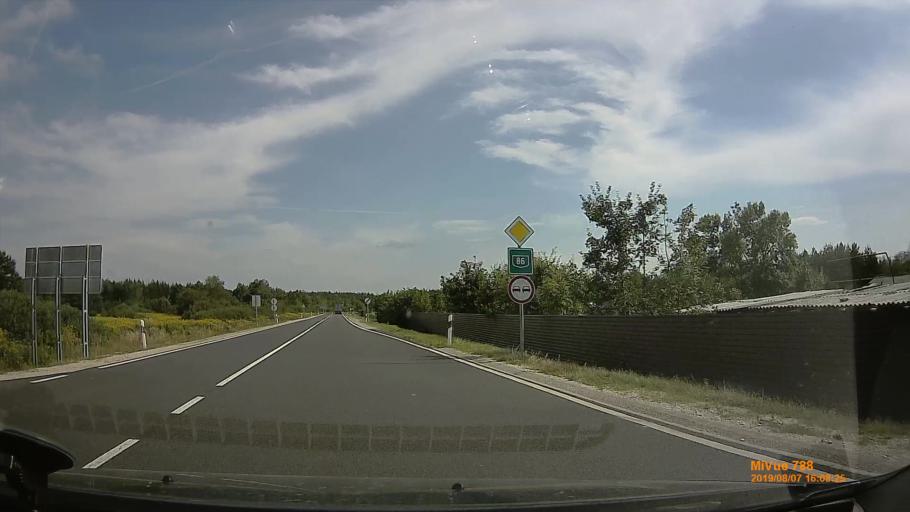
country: HU
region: Zala
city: Zalalovo
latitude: 46.9086
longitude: 16.6023
